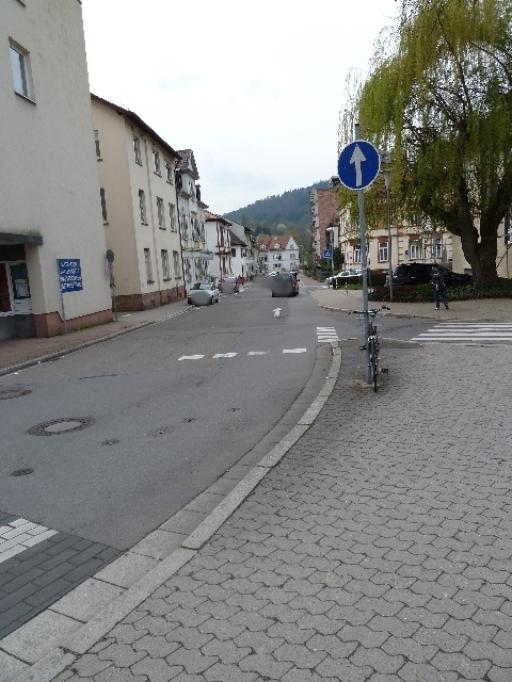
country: DE
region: Baden-Wuerttemberg
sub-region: Karlsruhe Region
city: Eberbach
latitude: 49.4651
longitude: 8.9843
